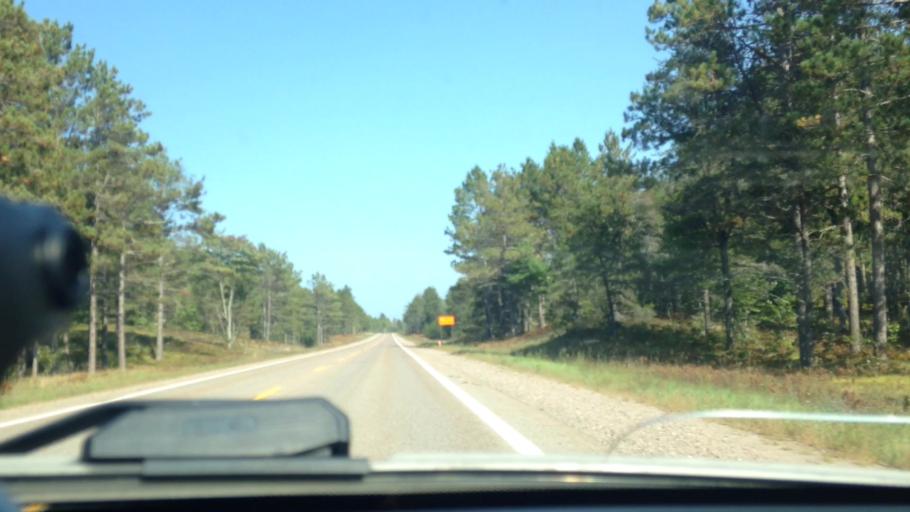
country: US
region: Michigan
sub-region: Mackinac County
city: Saint Ignace
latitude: 46.3533
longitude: -84.9016
